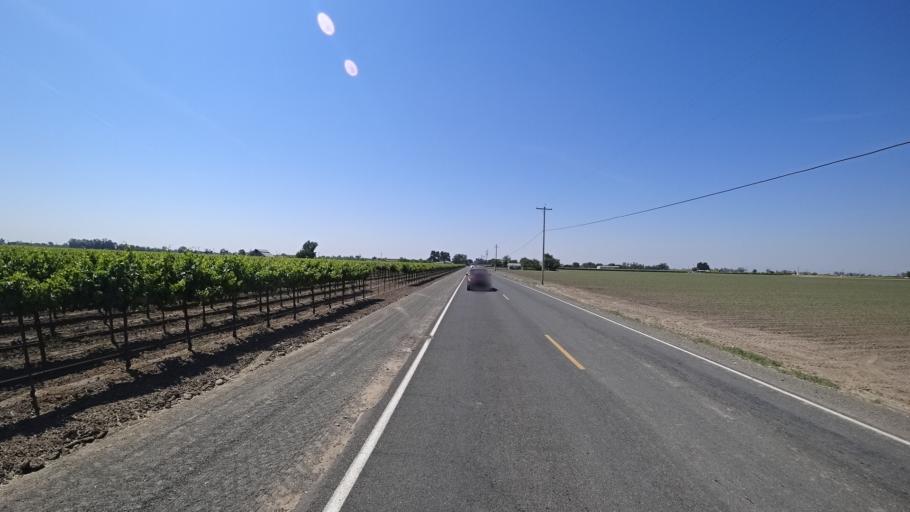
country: US
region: California
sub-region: Fresno County
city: Riverdale
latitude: 36.3690
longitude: -119.8513
